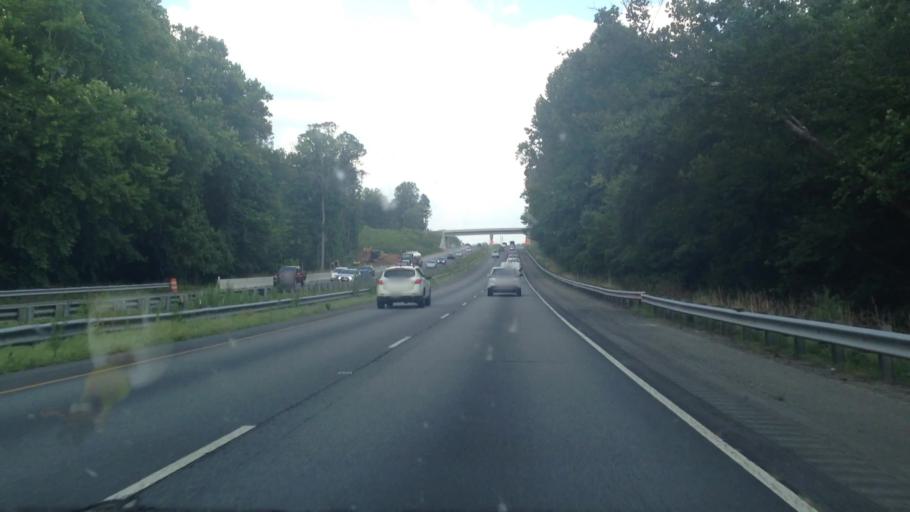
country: US
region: North Carolina
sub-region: Forsyth County
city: Walkertown
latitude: 36.1138
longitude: -80.1487
